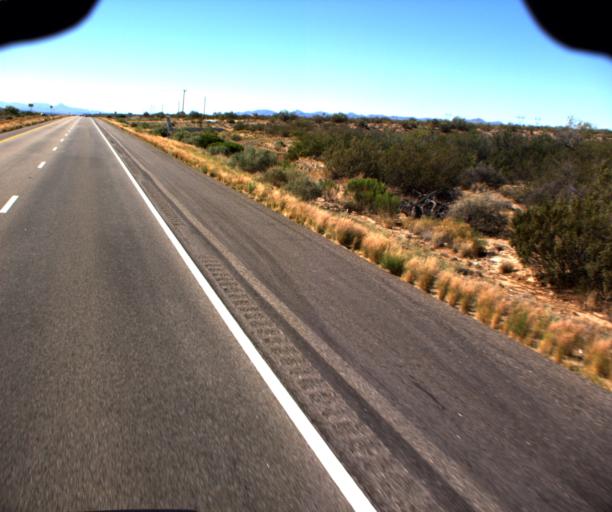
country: US
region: Arizona
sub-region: Mohave County
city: Kingman
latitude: 34.8551
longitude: -113.6396
